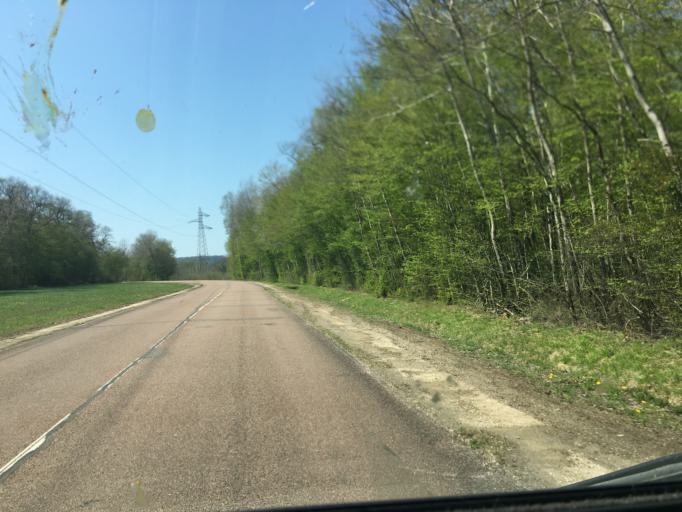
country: FR
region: Lorraine
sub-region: Departement de la Meuse
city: Vigneulles-les-Hattonchatel
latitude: 48.9482
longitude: 5.7292
